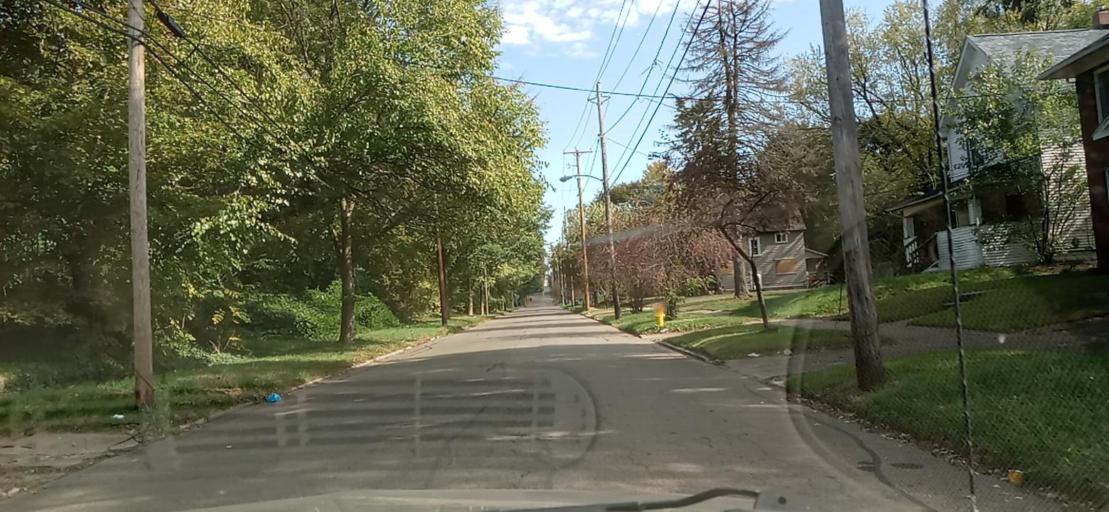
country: US
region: Ohio
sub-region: Summit County
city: Akron
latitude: 41.0562
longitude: -81.5387
